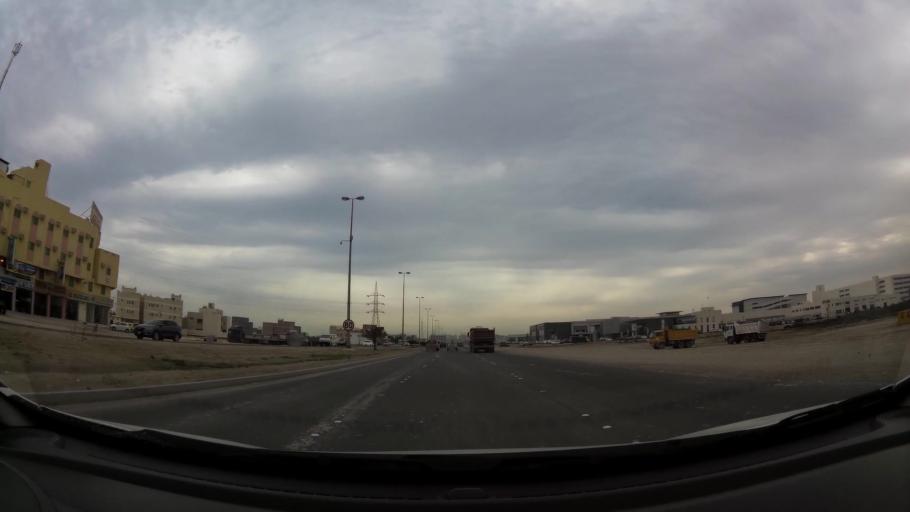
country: BH
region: Northern
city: Sitrah
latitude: 26.1565
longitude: 50.6081
